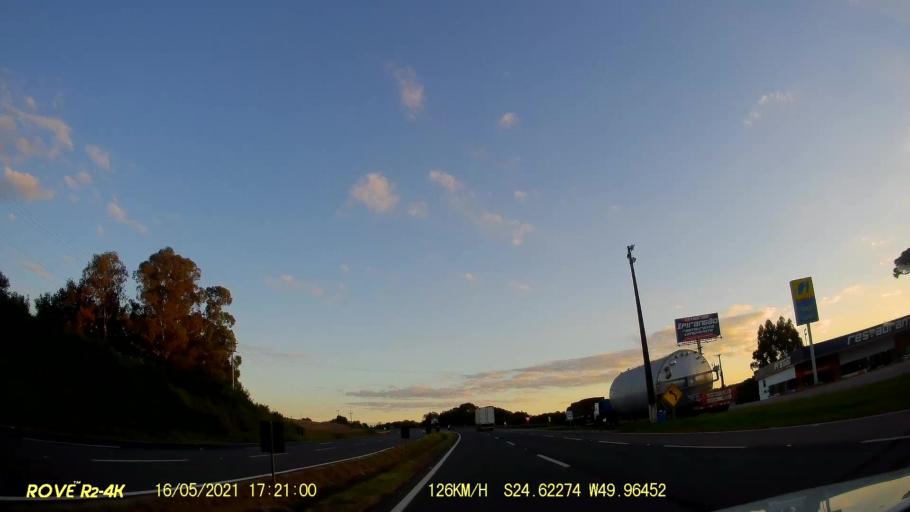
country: BR
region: Parana
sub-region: Pirai Do Sul
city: Pirai do Sul
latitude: -24.6232
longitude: -49.9648
